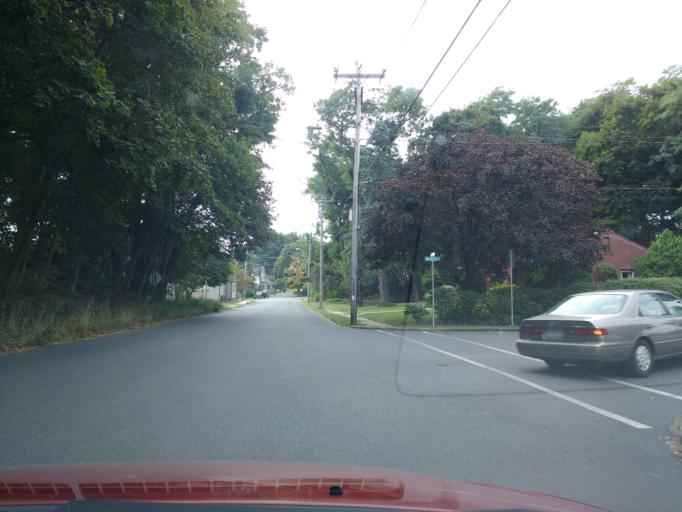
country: US
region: New York
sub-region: Ulster County
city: Kingston
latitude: 41.9204
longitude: -73.9944
